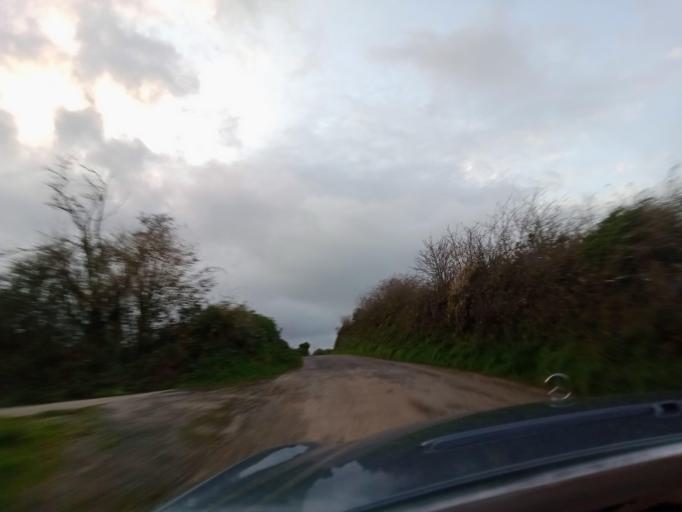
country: IE
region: Munster
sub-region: Waterford
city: Waterford
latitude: 52.3321
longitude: -7.0300
